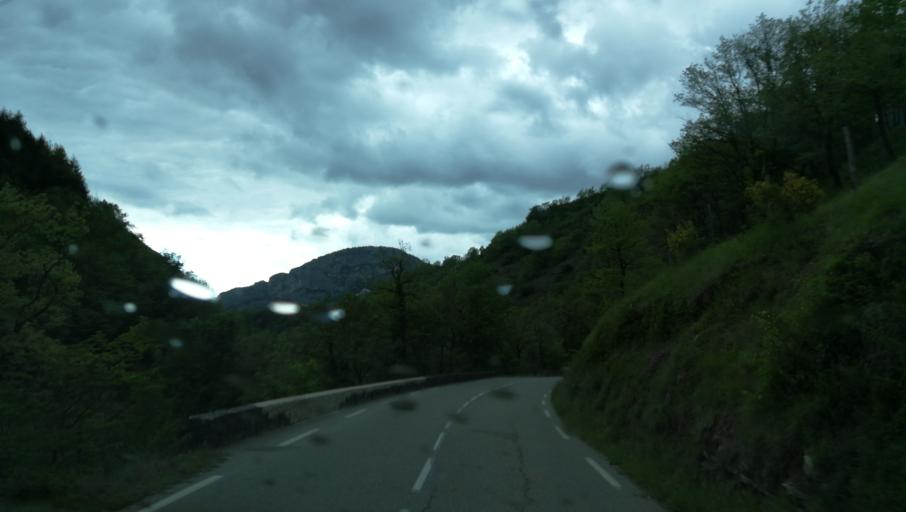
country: FR
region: Rhone-Alpes
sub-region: Departement de l'Isere
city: Pont-en-Royans
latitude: 45.0675
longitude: 5.3869
